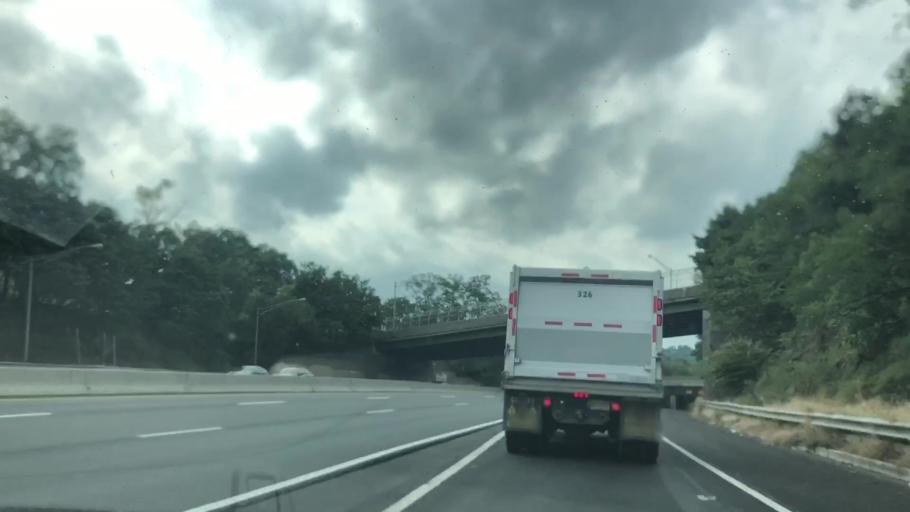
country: US
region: New Jersey
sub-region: Essex County
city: Orange
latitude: 40.7710
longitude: -74.2359
